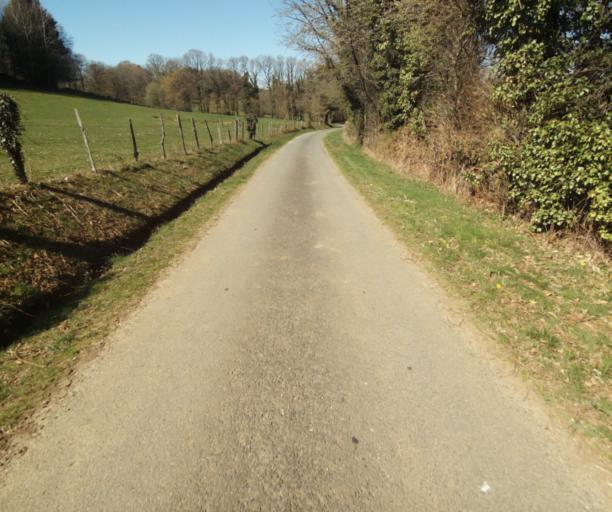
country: FR
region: Limousin
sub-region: Departement de la Correze
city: Saint-Clement
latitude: 45.3851
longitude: 1.6540
